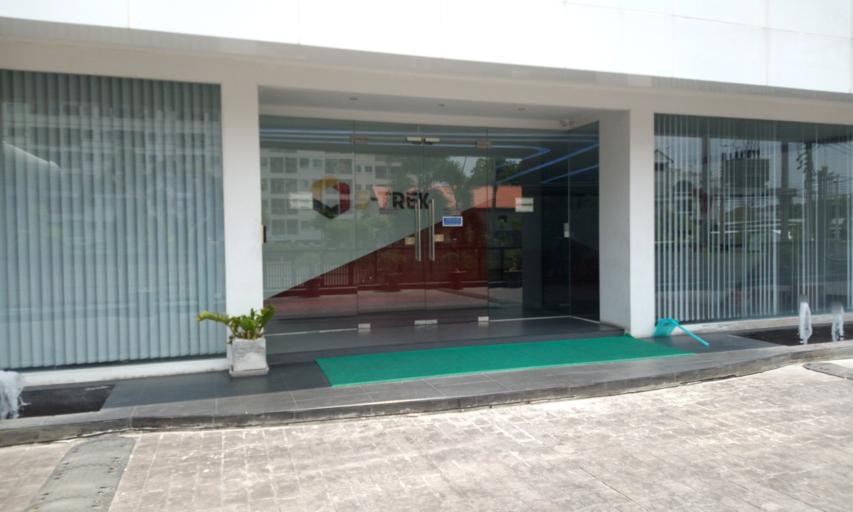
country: TH
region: Bangkok
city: Lat Phrao
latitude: 13.8267
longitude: 100.6241
